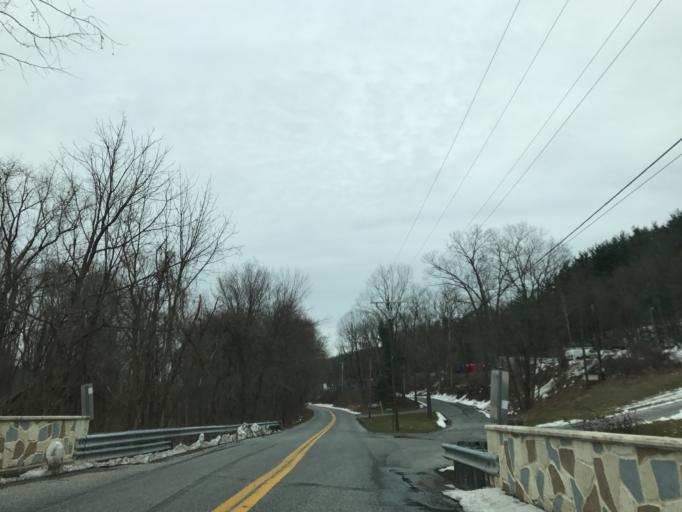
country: US
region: Maryland
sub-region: Baltimore County
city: Hunt Valley
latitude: 39.5435
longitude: -76.7332
